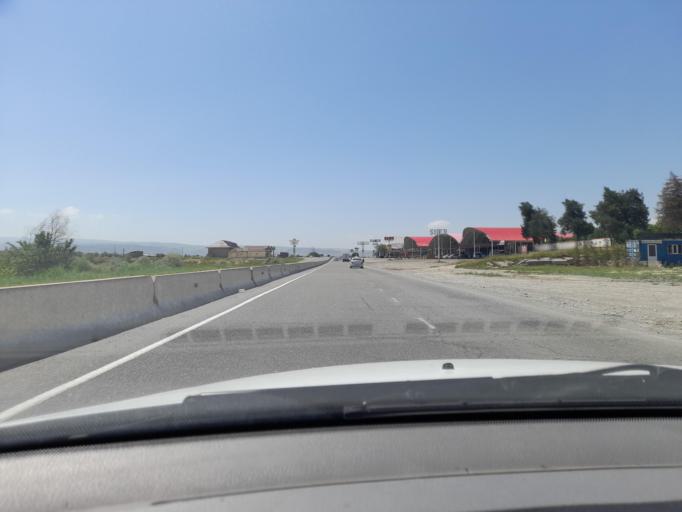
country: UZ
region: Jizzax
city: Jizzax
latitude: 40.0813
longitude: 67.9265
